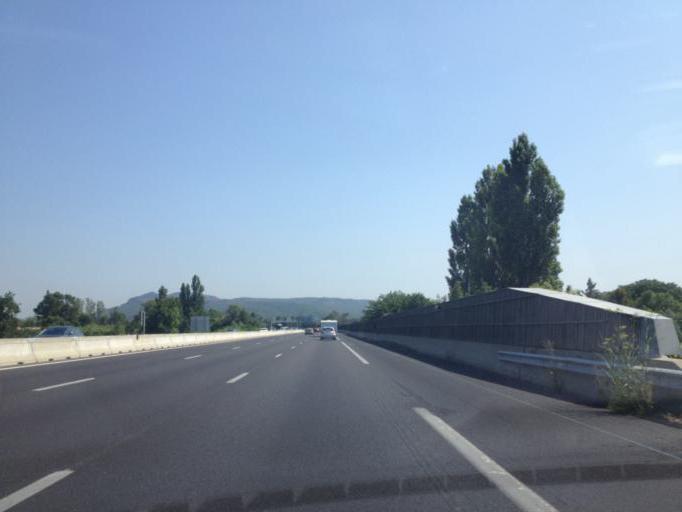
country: FR
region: Provence-Alpes-Cote d'Azur
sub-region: Departement du Vaucluse
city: Bollene
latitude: 44.2868
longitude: 4.7402
